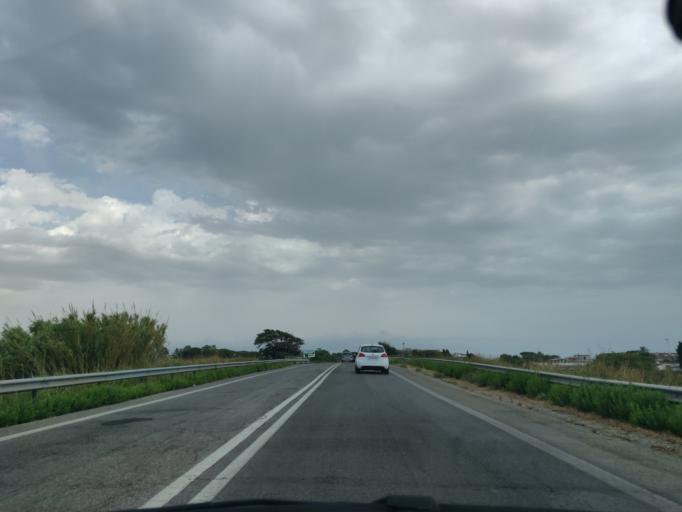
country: IT
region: Latium
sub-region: Citta metropolitana di Roma Capitale
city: Santa Marinella
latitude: 42.0355
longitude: 11.9267
